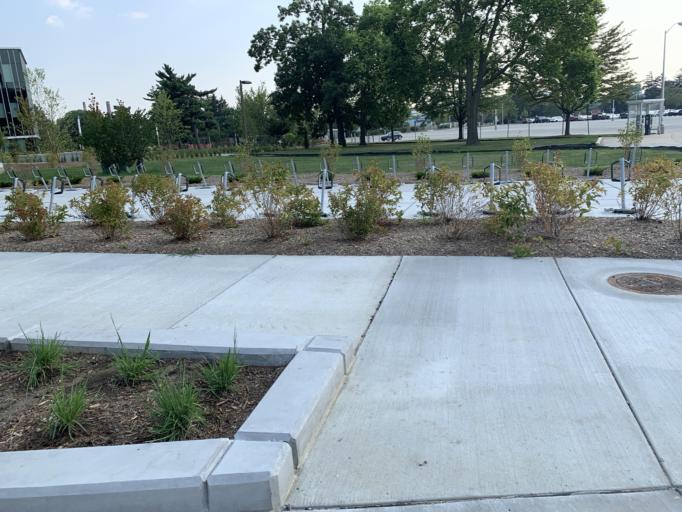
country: US
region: Michigan
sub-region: Ingham County
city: East Lansing
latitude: 42.7273
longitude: -84.4835
